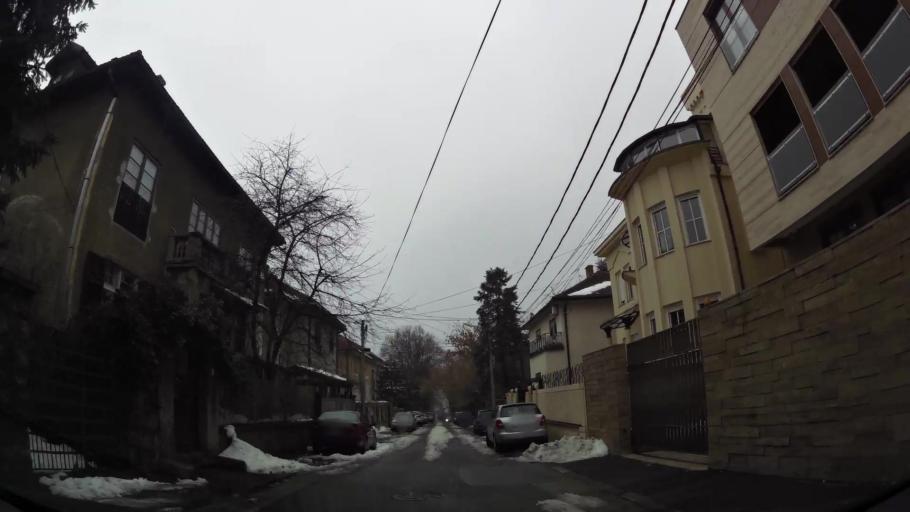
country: RS
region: Central Serbia
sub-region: Belgrade
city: Vozdovac
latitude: 44.7798
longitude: 20.4705
